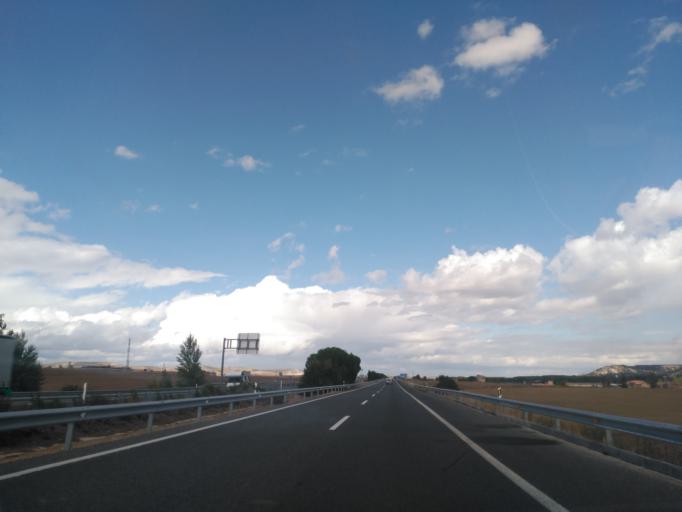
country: ES
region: Castille and Leon
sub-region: Provincia de Burgos
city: Villaquiran de los Infantes
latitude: 42.2244
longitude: -3.9994
